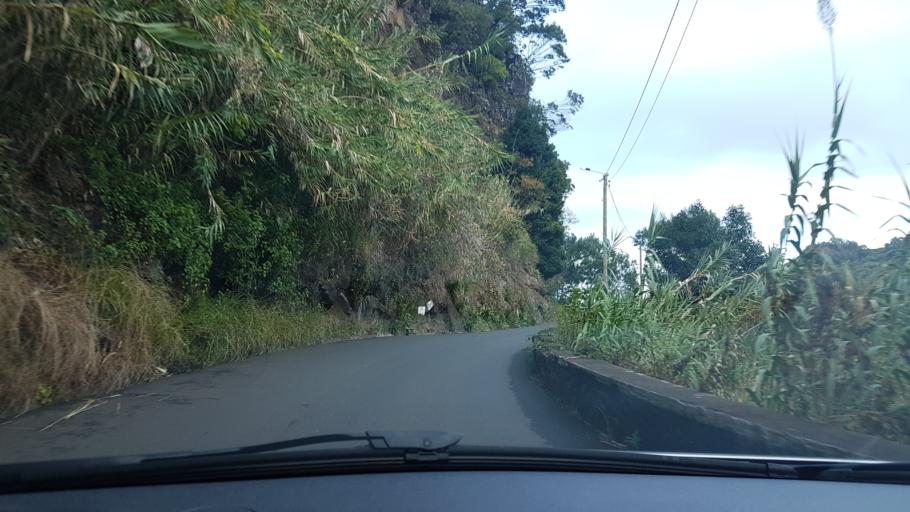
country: PT
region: Madeira
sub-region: Santana
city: Santana
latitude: 32.8221
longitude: -16.8998
